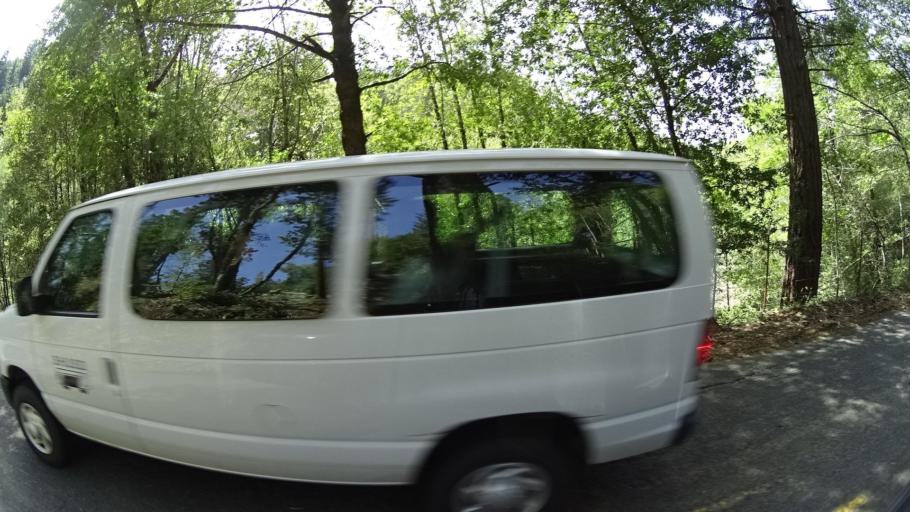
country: US
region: California
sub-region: Humboldt County
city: Redway
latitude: 40.3443
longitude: -123.7099
